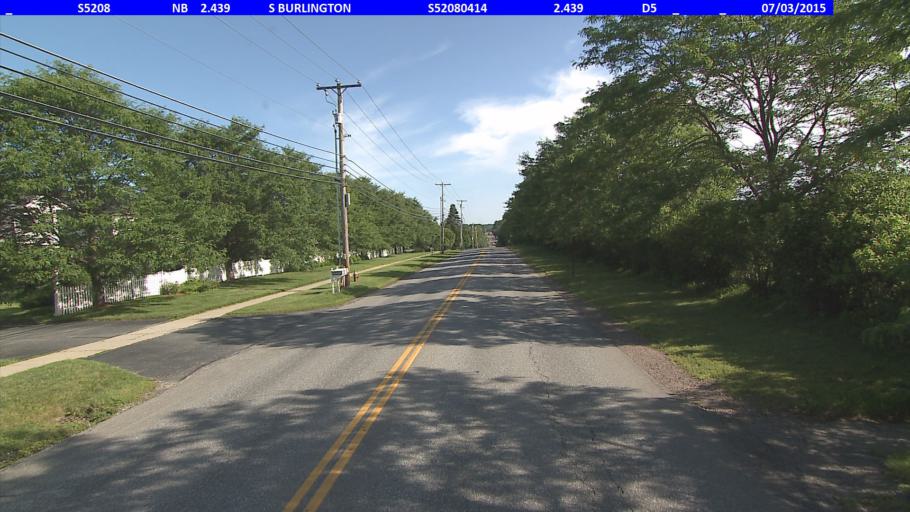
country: US
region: Vermont
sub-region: Chittenden County
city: South Burlington
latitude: 44.4455
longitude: -73.1774
